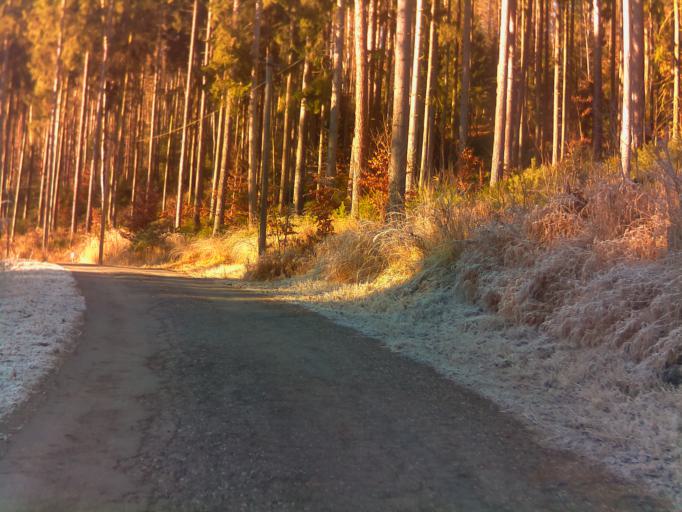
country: DE
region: Thuringia
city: Hummelshain
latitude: 50.7840
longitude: 11.6330
